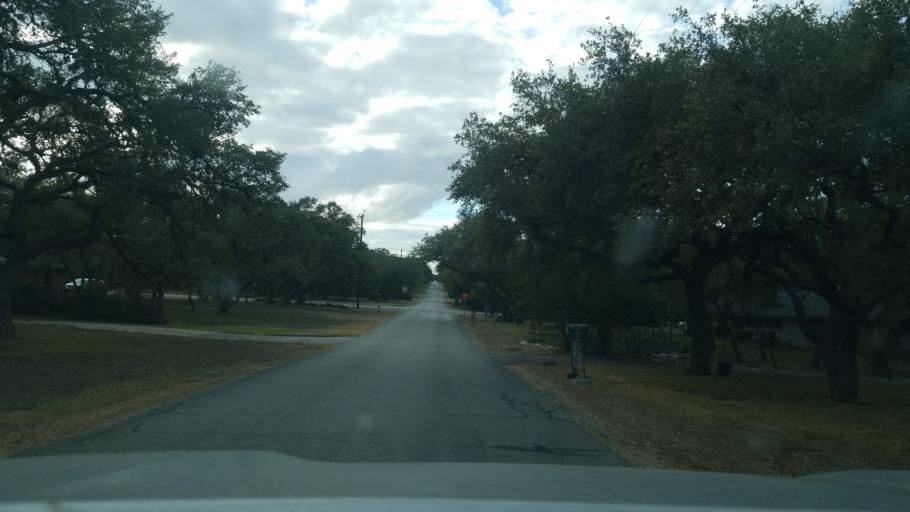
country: US
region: Texas
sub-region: Bexar County
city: Hollywood Park
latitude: 29.5984
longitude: -98.4811
